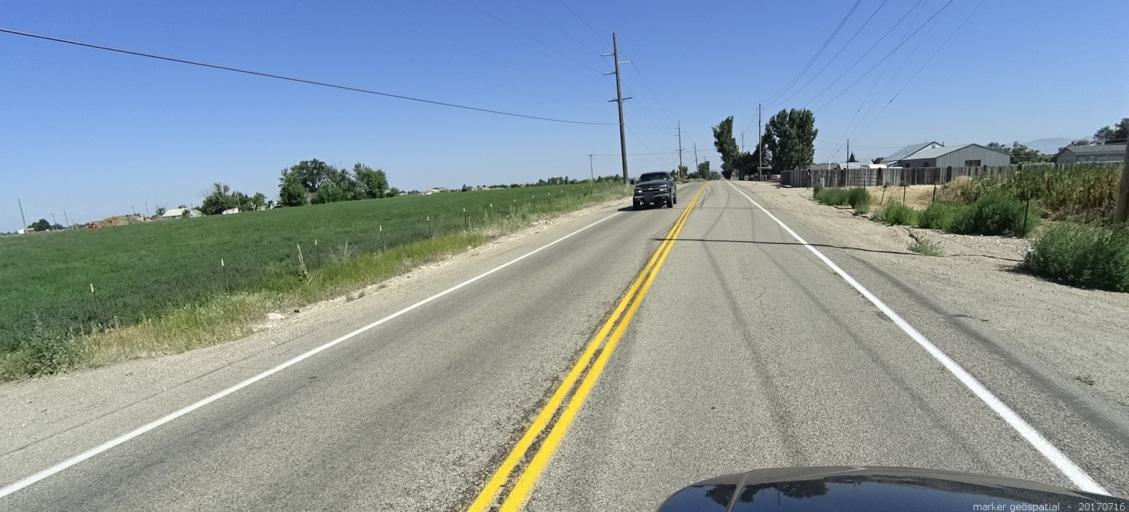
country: US
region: Idaho
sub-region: Ada County
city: Kuna
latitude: 43.5155
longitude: -116.3345
